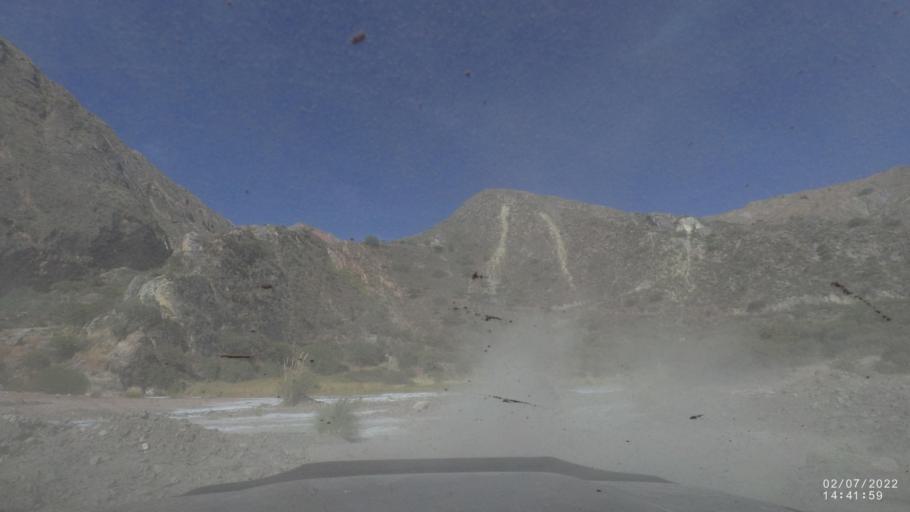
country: BO
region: Cochabamba
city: Irpa Irpa
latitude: -17.8505
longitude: -66.4202
